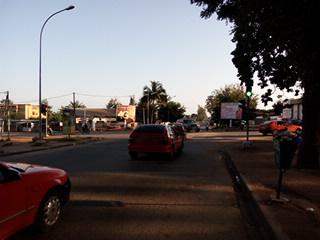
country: CI
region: Vallee du Bandama
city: Bouake
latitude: 7.6848
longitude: -5.0260
